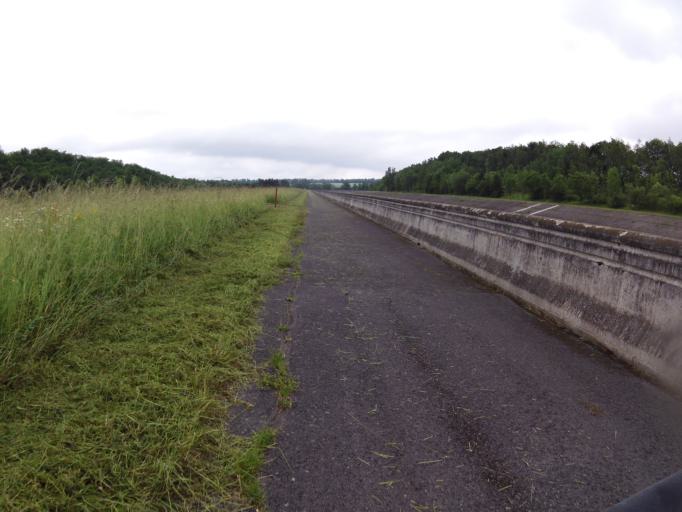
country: FR
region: Champagne-Ardenne
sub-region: Departement de la Haute-Marne
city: Villiers-en-Lieu
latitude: 48.6088
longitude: 4.8648
